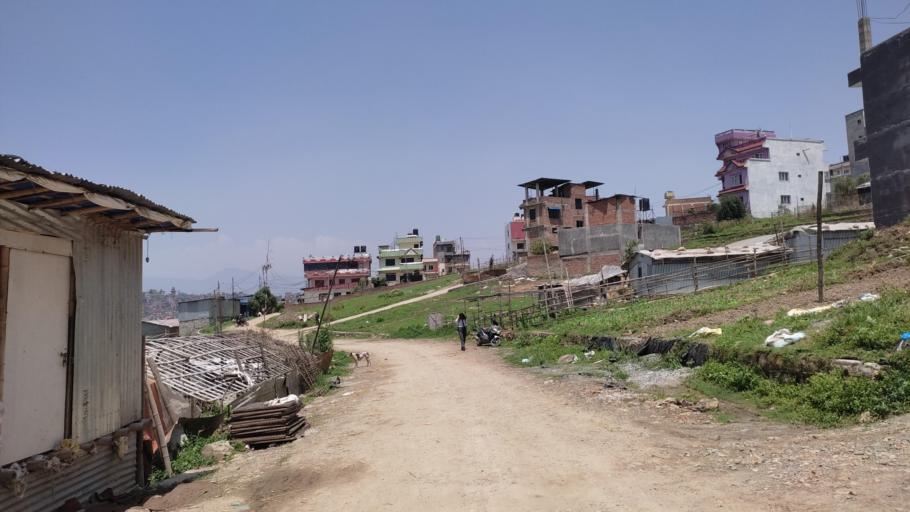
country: NP
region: Central Region
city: Kirtipur
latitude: 27.6690
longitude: 85.2669
